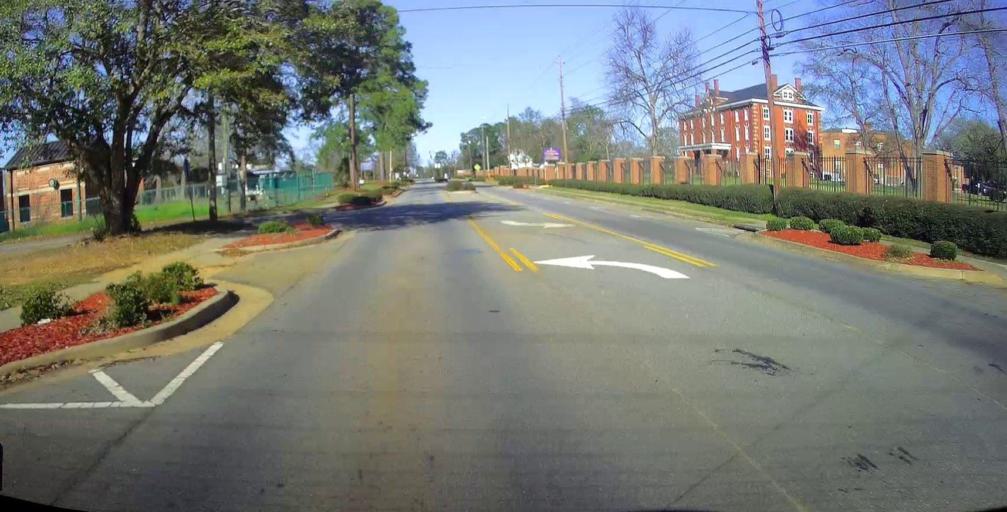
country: US
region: Georgia
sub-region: Peach County
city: Fort Valley
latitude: 32.5396
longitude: -83.8975
